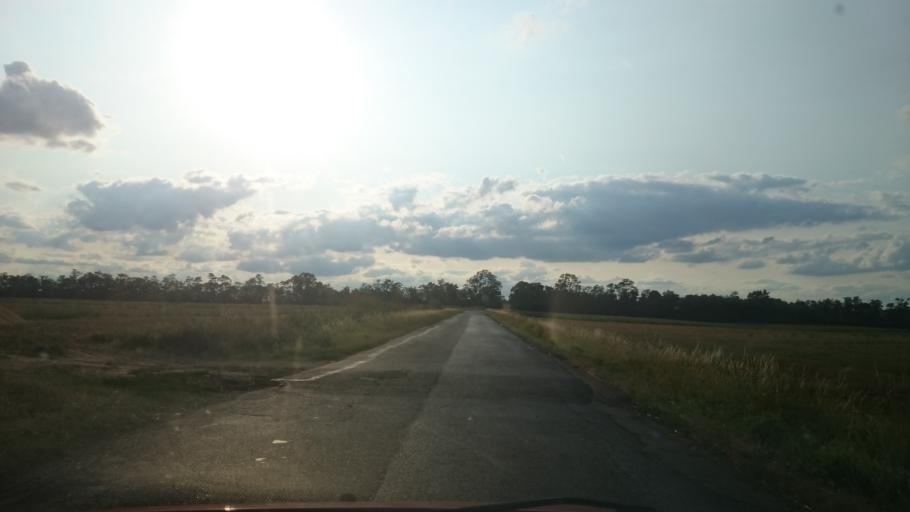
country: PL
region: Opole Voivodeship
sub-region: Powiat nyski
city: Otmuchow
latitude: 50.5067
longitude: 17.1623
